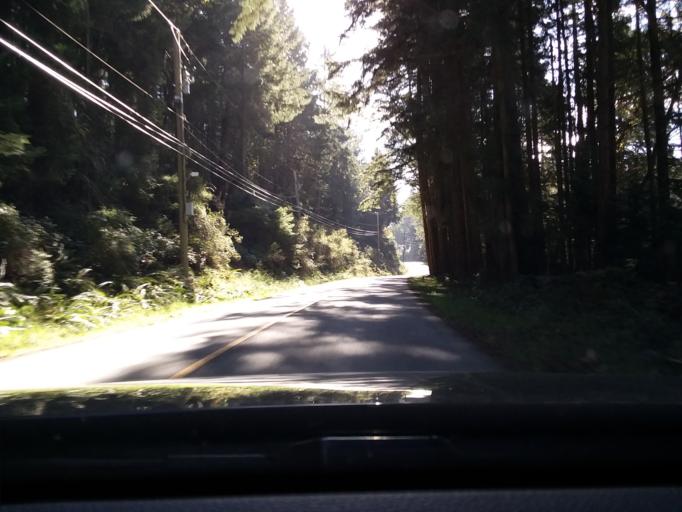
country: CA
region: British Columbia
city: North Cowichan
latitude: 48.9472
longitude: -123.5132
